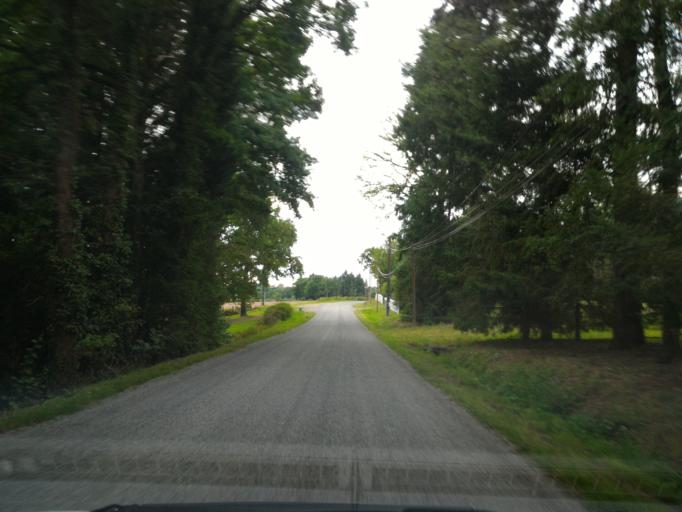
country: FR
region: Limousin
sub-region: Departement de la Haute-Vienne
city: Saint-Junien
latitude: 45.9026
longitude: 0.8670
